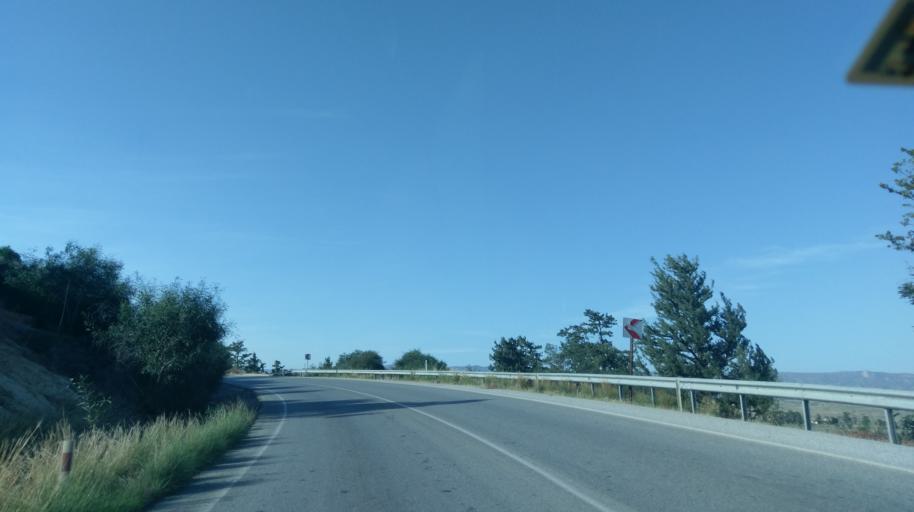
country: CY
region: Ammochostos
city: Trikomo
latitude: 35.2787
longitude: 33.8494
